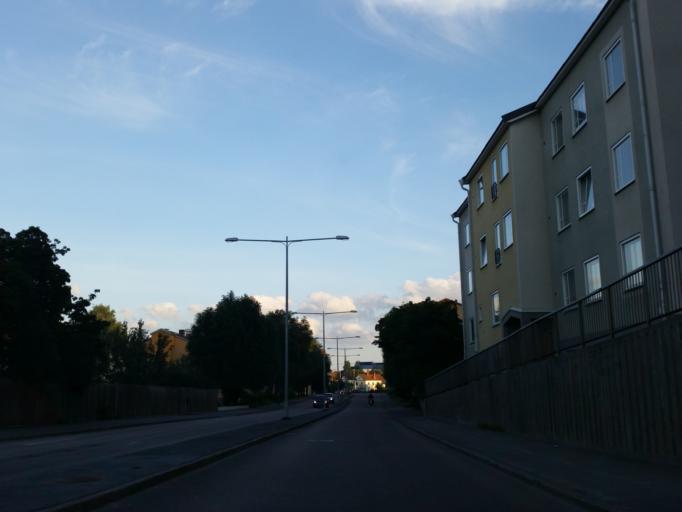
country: SE
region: Stockholm
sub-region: Sodertalje Kommun
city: Soedertaelje
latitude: 59.2000
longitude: 17.6179
